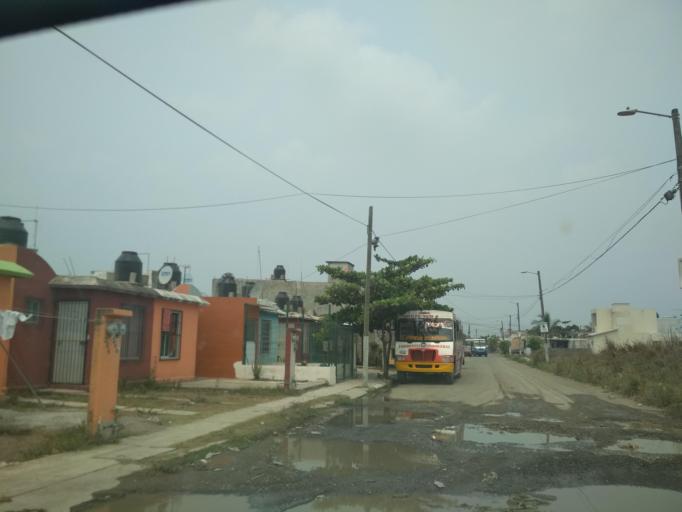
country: MX
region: Veracruz
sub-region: Veracruz
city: Arboledas
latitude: 19.2068
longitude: -96.2133
